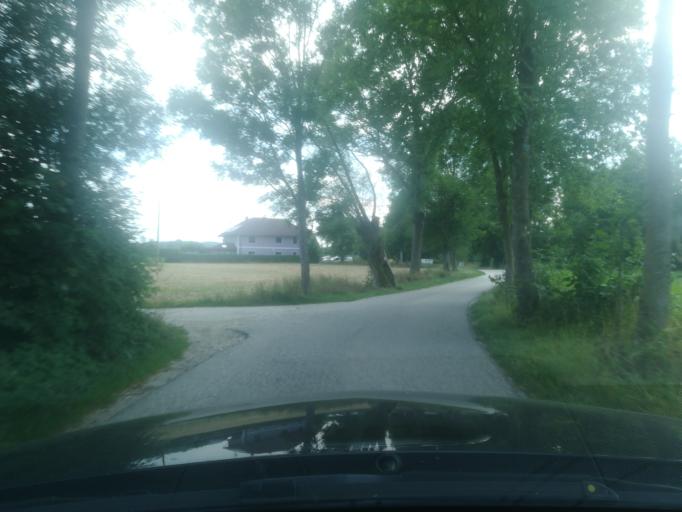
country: AT
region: Upper Austria
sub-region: Wels-Land
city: Marchtrenk
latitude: 48.1836
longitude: 14.1233
